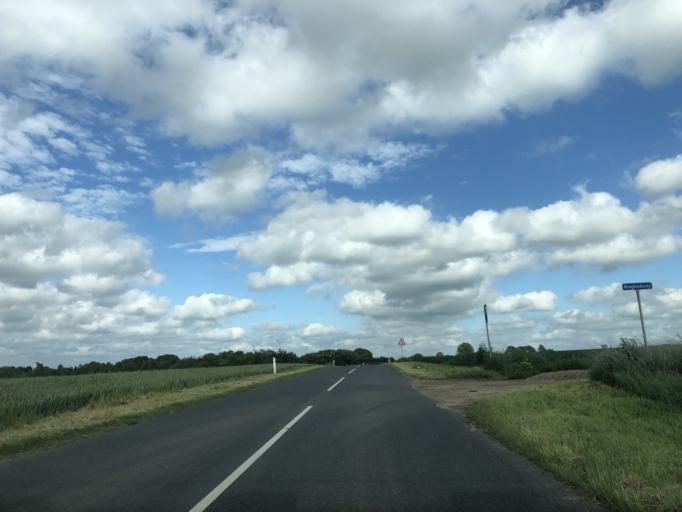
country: DK
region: Central Jutland
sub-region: Viborg Kommune
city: Bjerringbro
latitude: 56.3533
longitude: 9.7072
